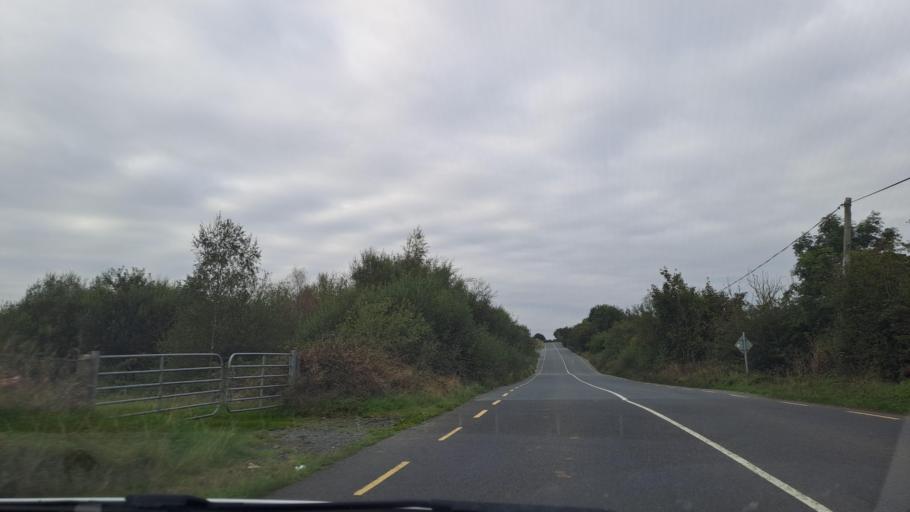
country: IE
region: Ulster
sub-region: County Monaghan
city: Carrickmacross
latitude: 54.0297
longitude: -6.7761
